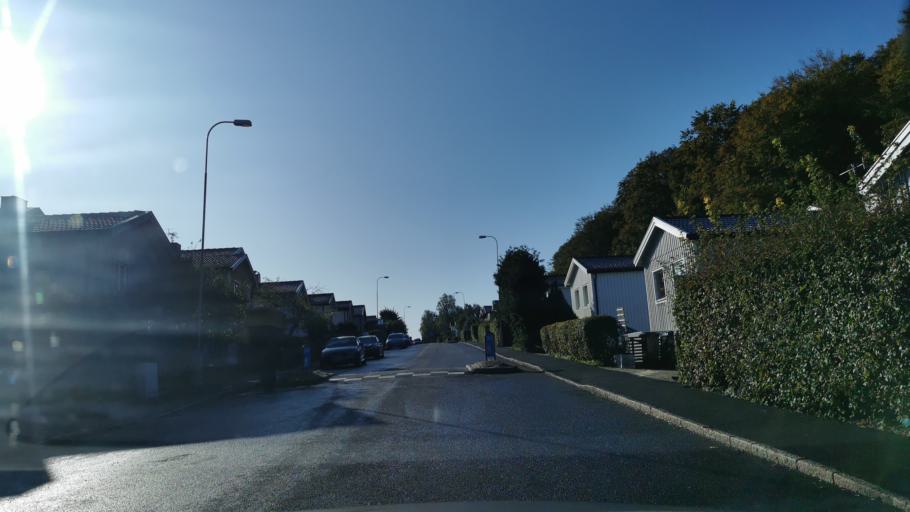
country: SE
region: Vaestra Goetaland
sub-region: Goteborg
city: Eriksbo
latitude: 57.7270
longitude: 12.0517
